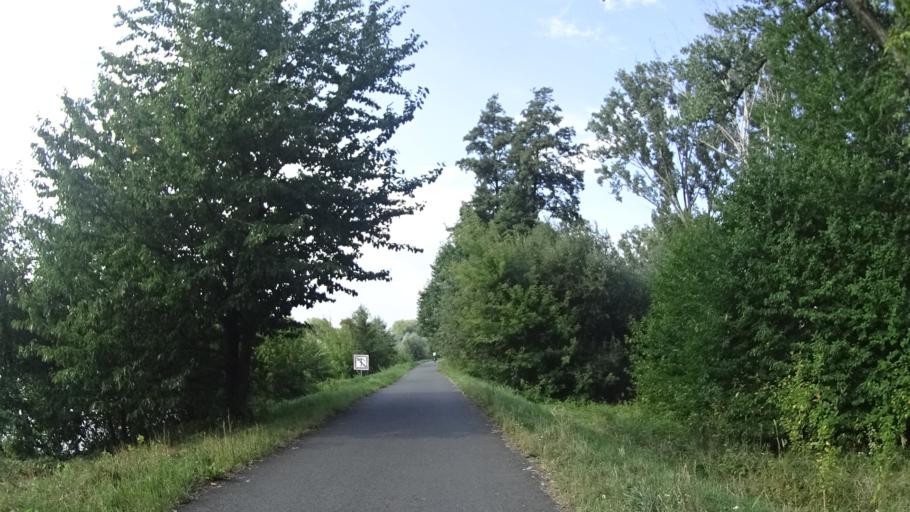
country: CZ
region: Zlin
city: Spytihnev
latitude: 49.1477
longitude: 17.5054
